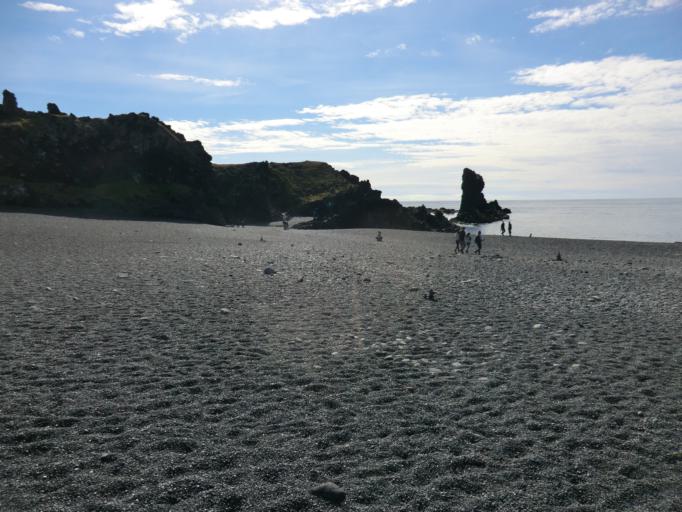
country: IS
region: West
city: Olafsvik
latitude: 64.7522
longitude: -23.9009
